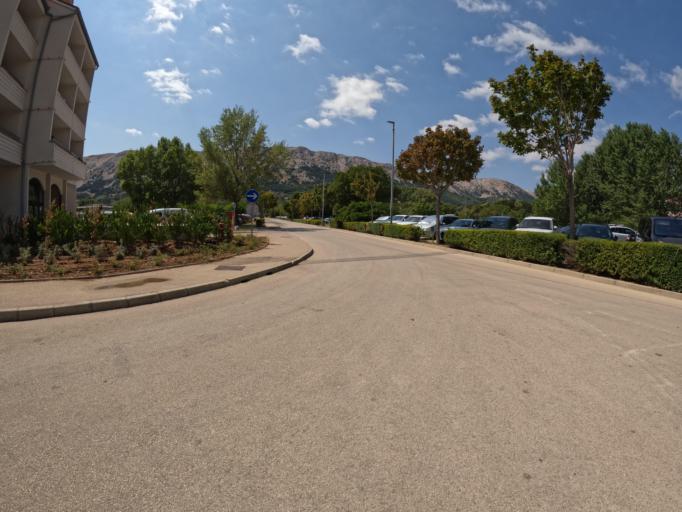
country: HR
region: Primorsko-Goranska
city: Punat
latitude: 44.9685
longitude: 14.7485
